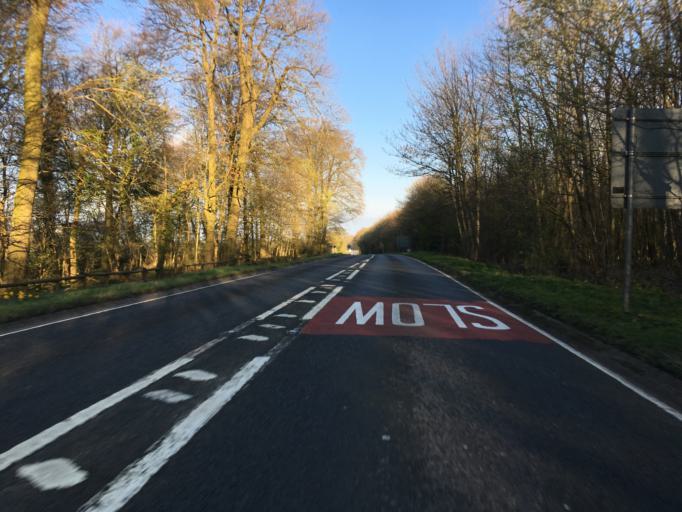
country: GB
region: England
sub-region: Gloucestershire
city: Bourton on the Water
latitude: 51.8232
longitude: -1.7785
